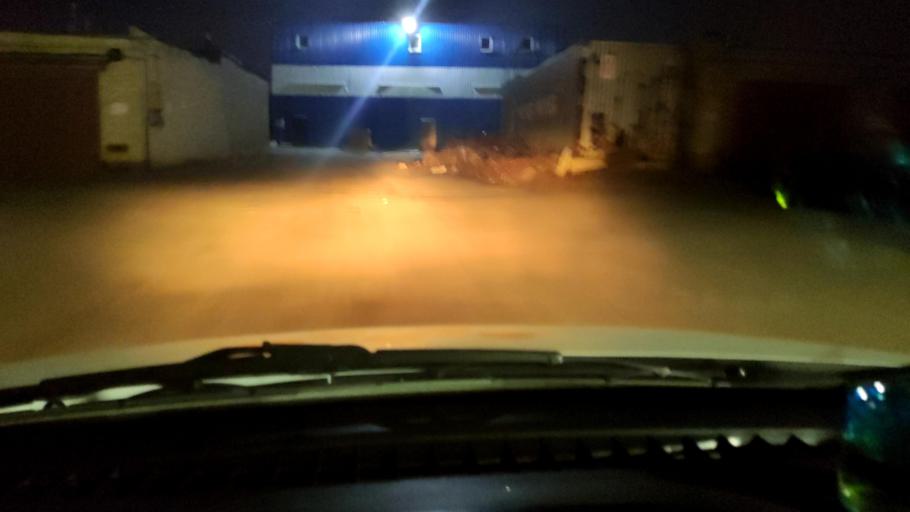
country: RU
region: Voronezj
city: Voronezh
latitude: 51.6374
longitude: 39.1303
